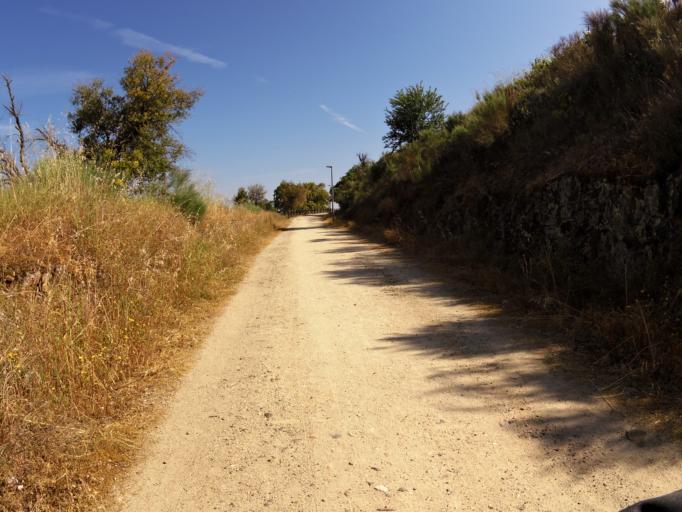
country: PT
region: Braganca
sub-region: Torre de Moncorvo
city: Torre de Moncorvo
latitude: 41.1805
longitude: -7.0340
